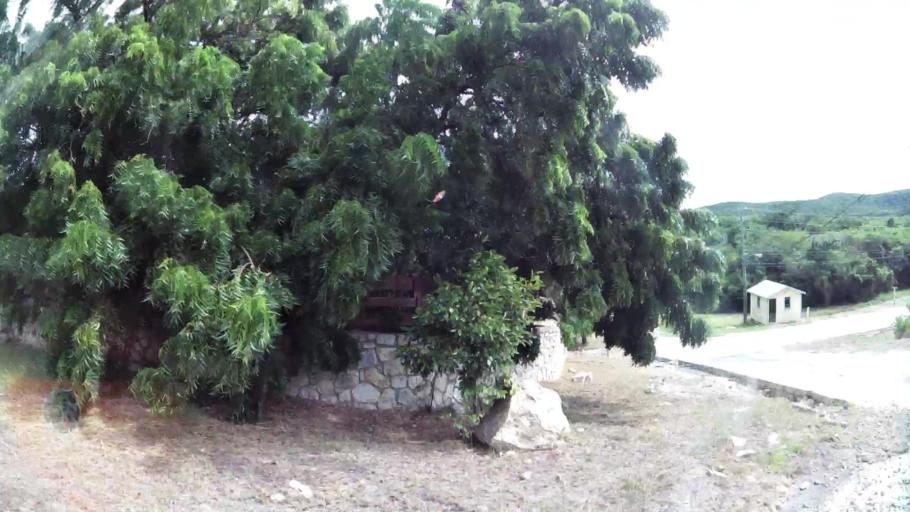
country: AG
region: Saint Peter
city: Parham
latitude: 17.0661
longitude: -61.6975
